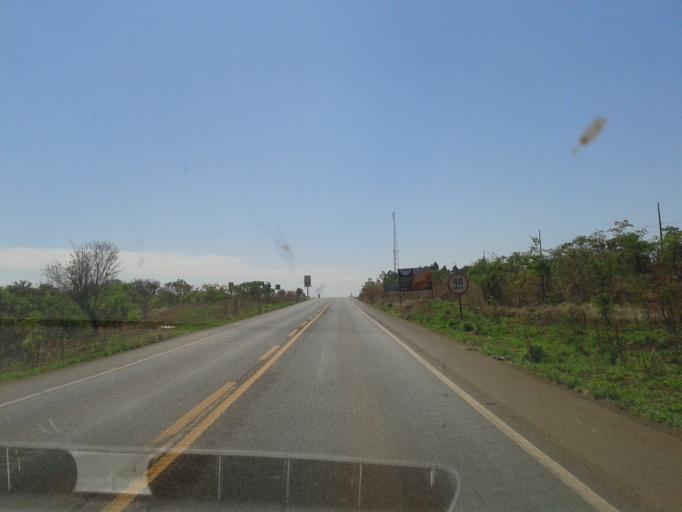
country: BR
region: Minas Gerais
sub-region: Sacramento
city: Sacramento
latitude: -19.3192
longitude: -47.5511
